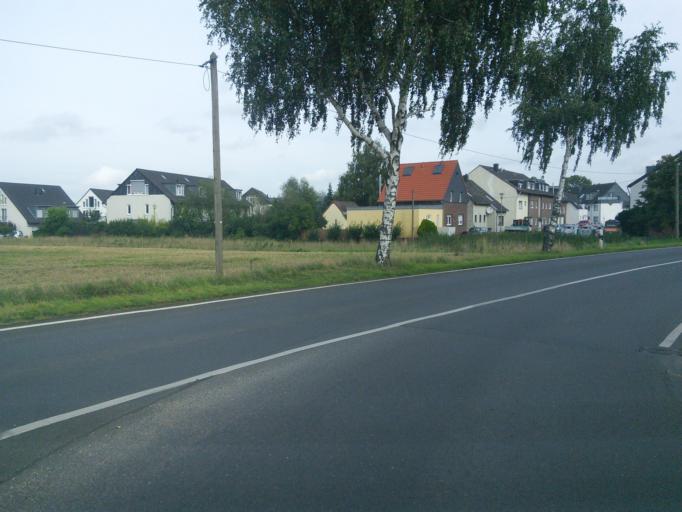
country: DE
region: North Rhine-Westphalia
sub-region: Regierungsbezirk Koln
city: Mengenich
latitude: 50.9599
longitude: 6.8293
